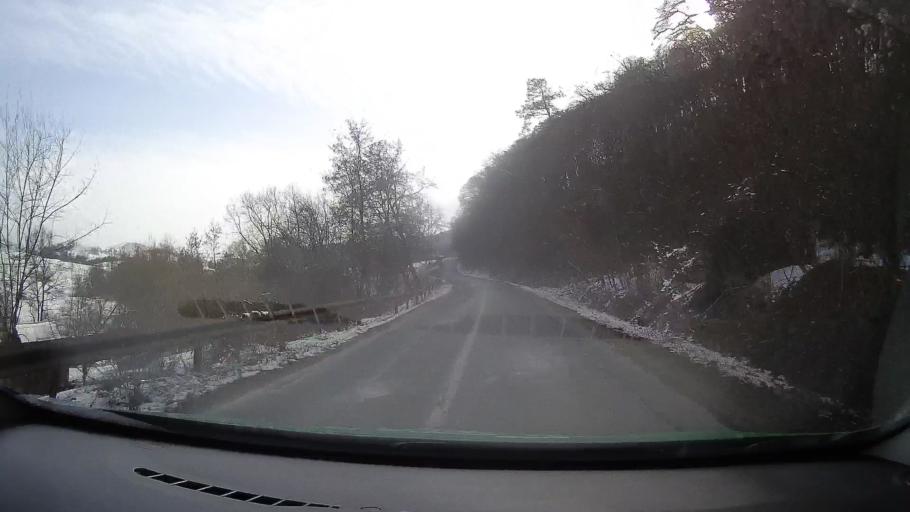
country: RO
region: Mures
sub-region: Comuna Apold
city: Saes
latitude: 46.1788
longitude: 24.7575
